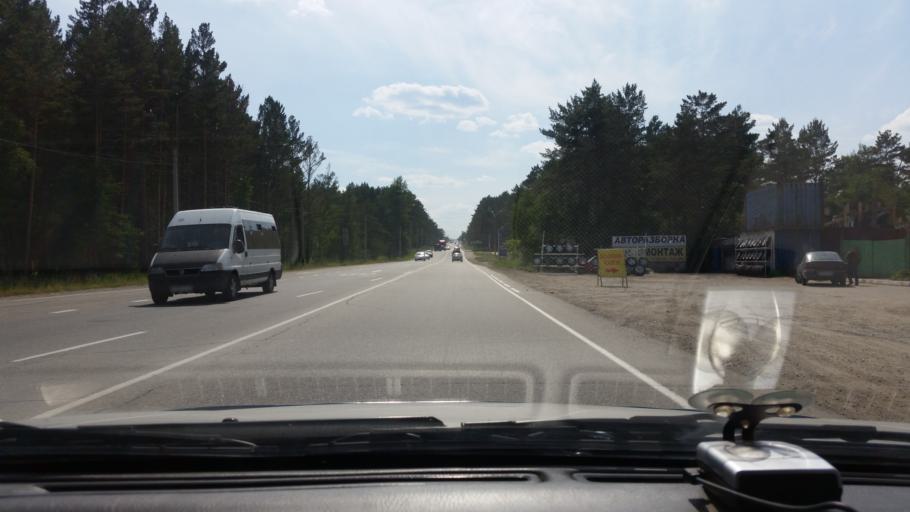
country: RU
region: Irkutsk
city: Shelekhov
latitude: 52.2157
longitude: 104.1232
